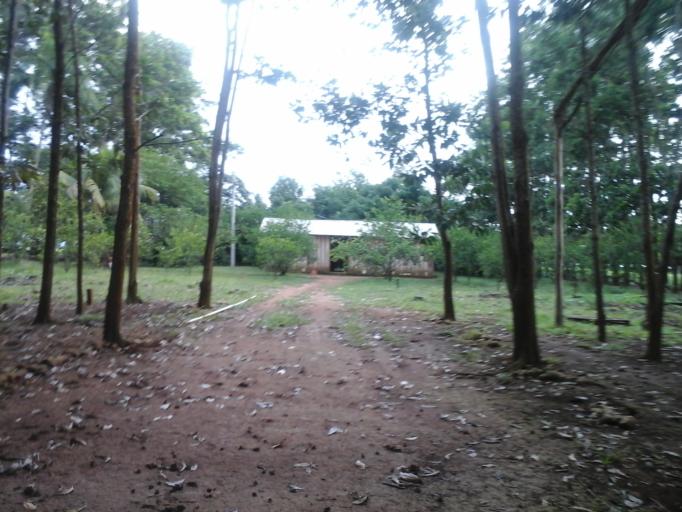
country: CO
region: Cundinamarca
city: Tibacuy
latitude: 4.2139
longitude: -72.4579
